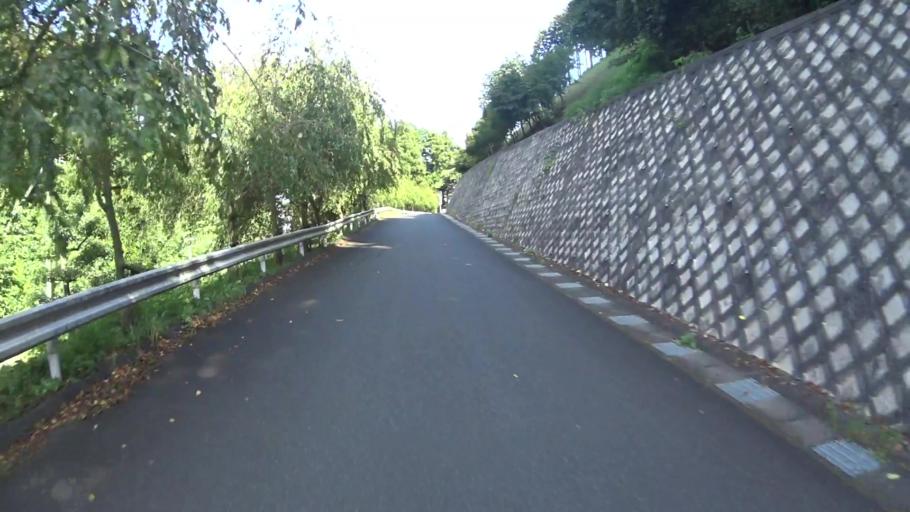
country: JP
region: Kyoto
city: Miyazu
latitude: 35.5652
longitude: 135.1344
